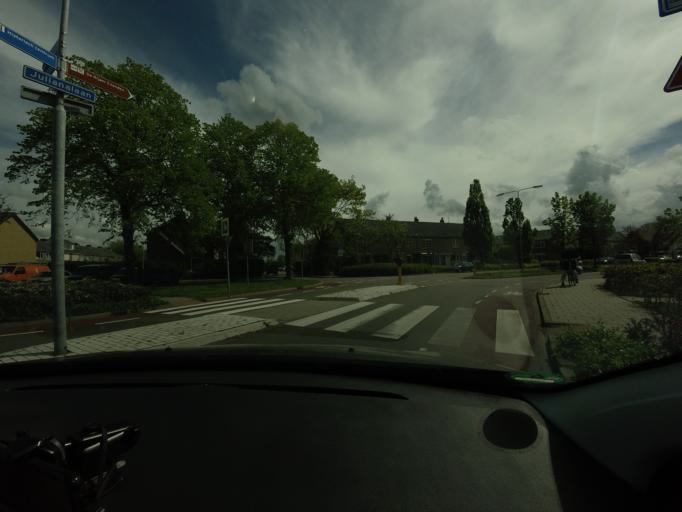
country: NL
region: North Holland
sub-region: Gemeente Beemster
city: Halfweg
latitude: 52.5539
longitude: 4.8450
